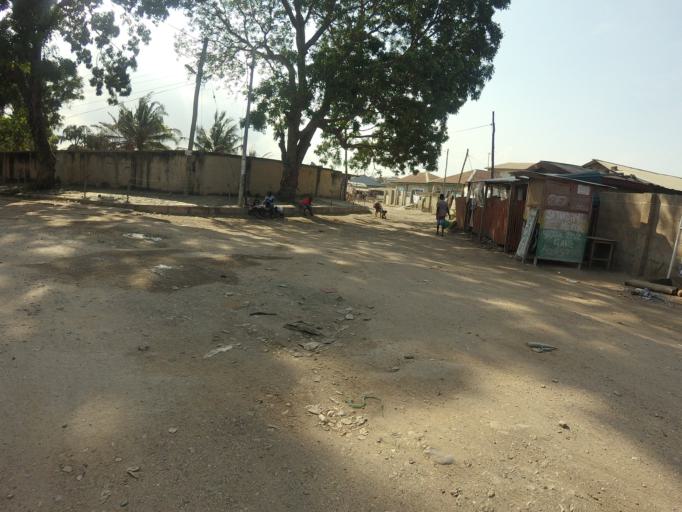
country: GH
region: Greater Accra
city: Dome
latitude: 5.6535
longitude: -0.2651
